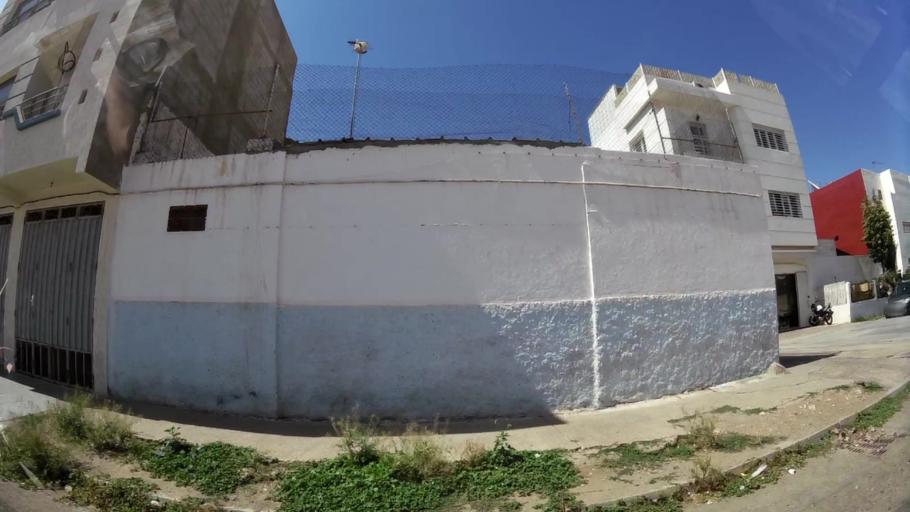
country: MA
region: Souss-Massa-Draa
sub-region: Agadir-Ida-ou-Tnan
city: Agadir
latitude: 30.4095
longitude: -9.5862
